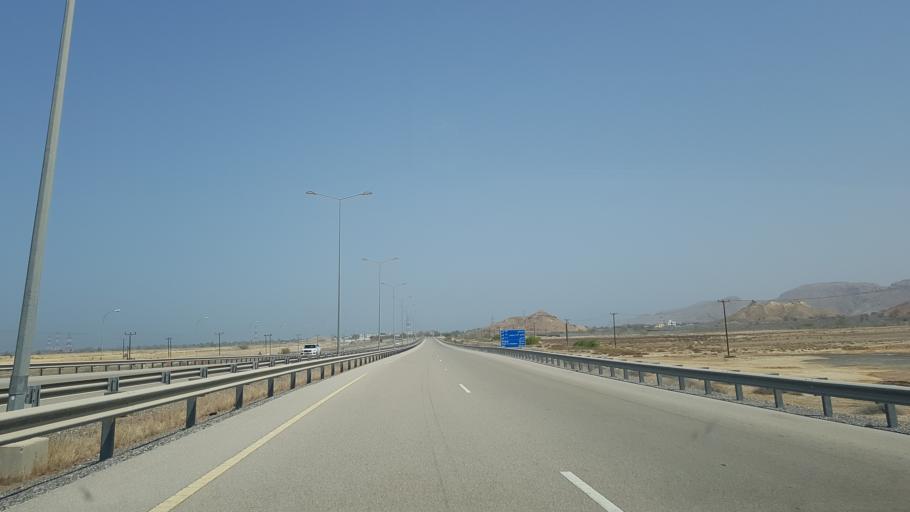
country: OM
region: Muhafazat Masqat
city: Muscat
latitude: 23.2128
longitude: 58.9373
